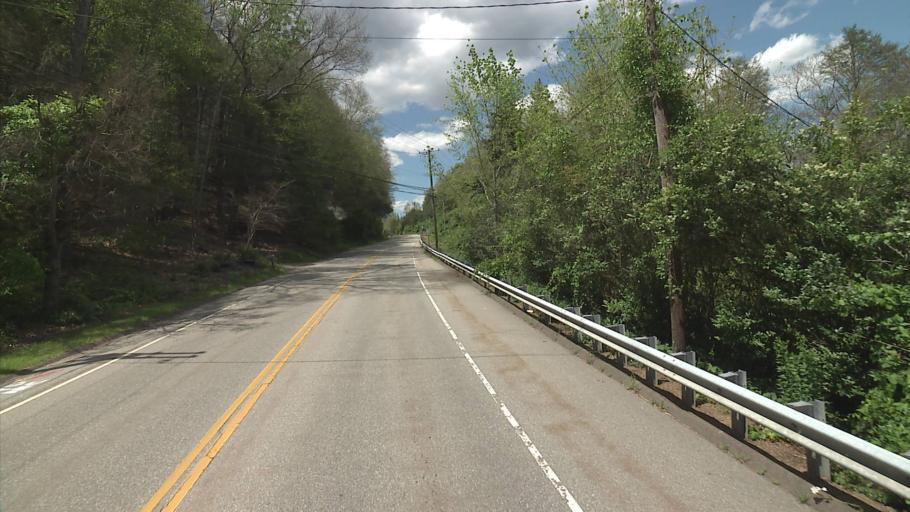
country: US
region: Connecticut
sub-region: Middlesex County
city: Moodus
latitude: 41.5150
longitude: -72.4836
